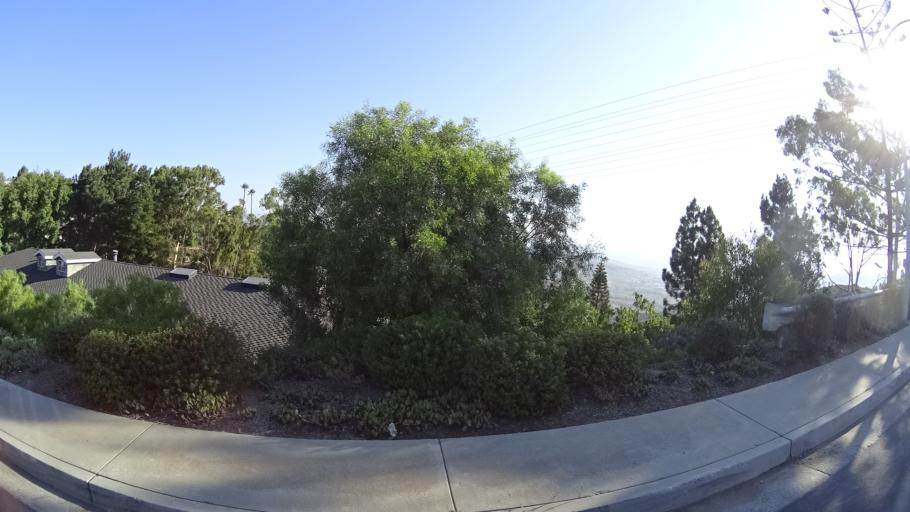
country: US
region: California
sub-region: Orange County
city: San Clemente
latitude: 33.4170
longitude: -117.5886
